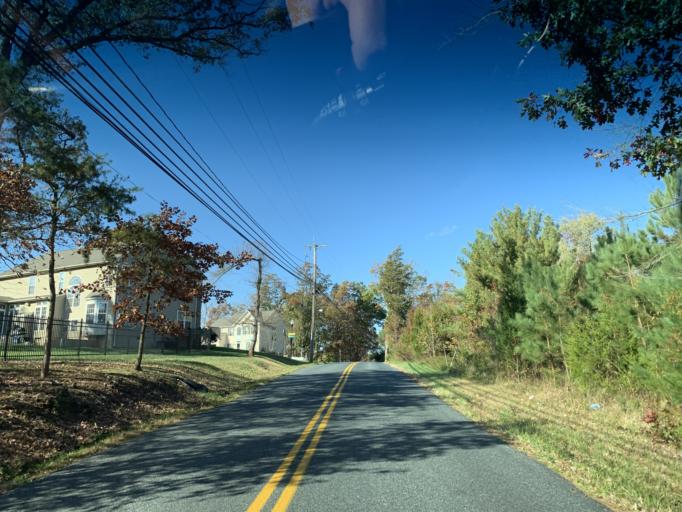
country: US
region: Maryland
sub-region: Harford County
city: Joppatowne
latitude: 39.4414
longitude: -76.3329
